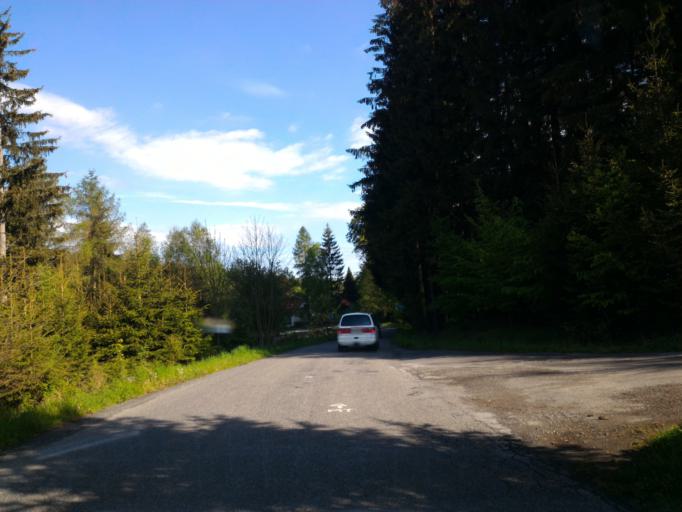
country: CZ
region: Vysocina
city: Ledec nad Sazavou
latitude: 49.6359
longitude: 15.3019
